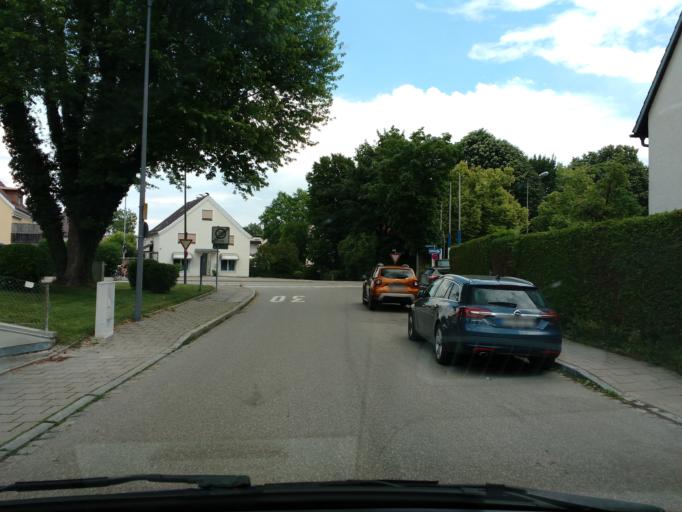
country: DE
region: Bavaria
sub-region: Upper Bavaria
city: Rosenheim
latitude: 47.8669
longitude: 12.1205
